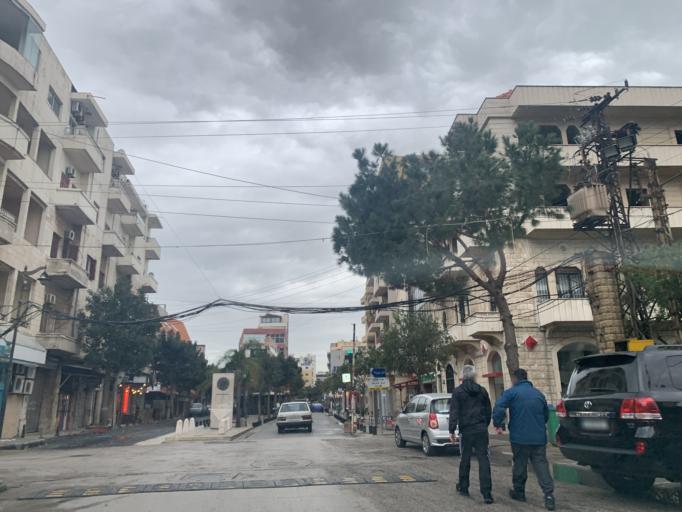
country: LB
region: Mont-Liban
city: Djounie
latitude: 33.9850
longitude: 35.6340
